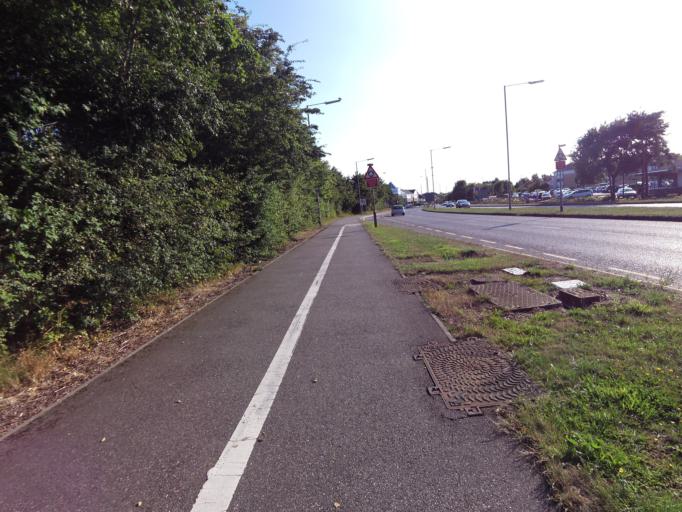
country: GB
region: England
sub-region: Essex
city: Chelmsford
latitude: 51.7463
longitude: 0.5017
